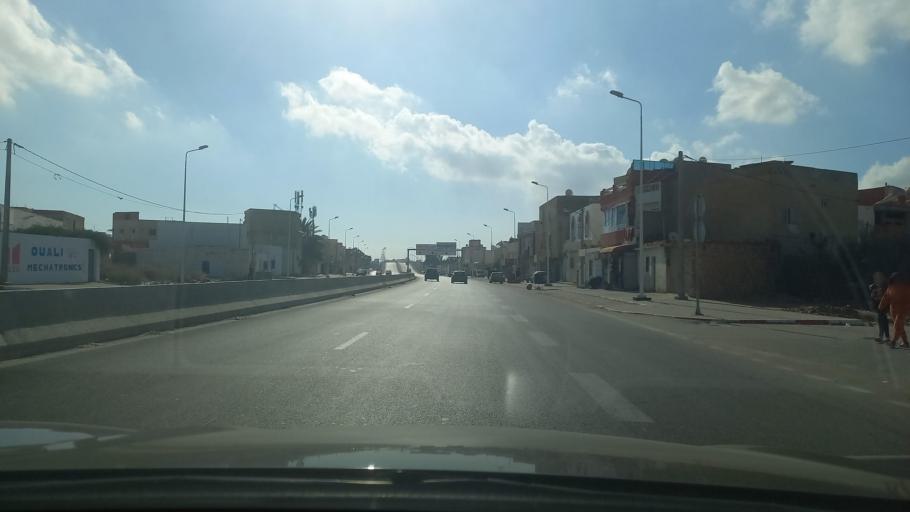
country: TN
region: Safaqis
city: Sfax
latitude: 34.7379
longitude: 10.7237
